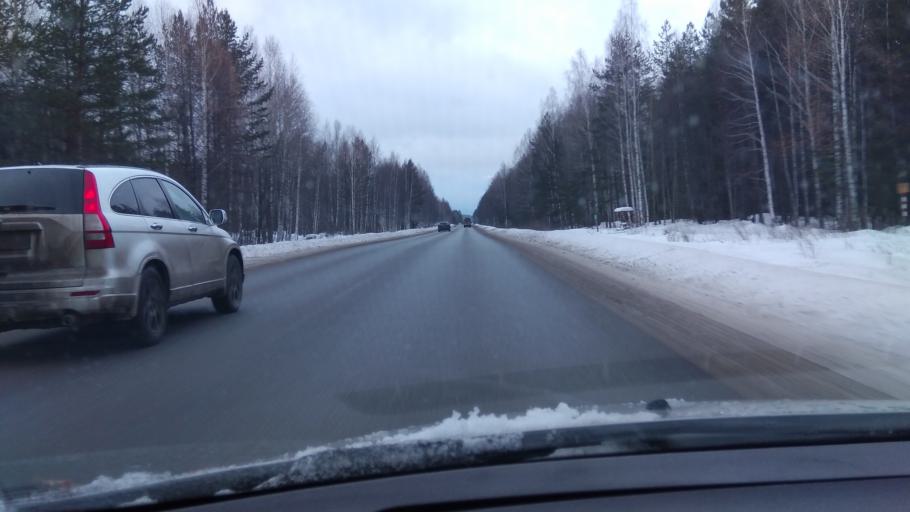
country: RU
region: Sverdlovsk
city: Iset'
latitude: 57.1110
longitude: 60.3399
